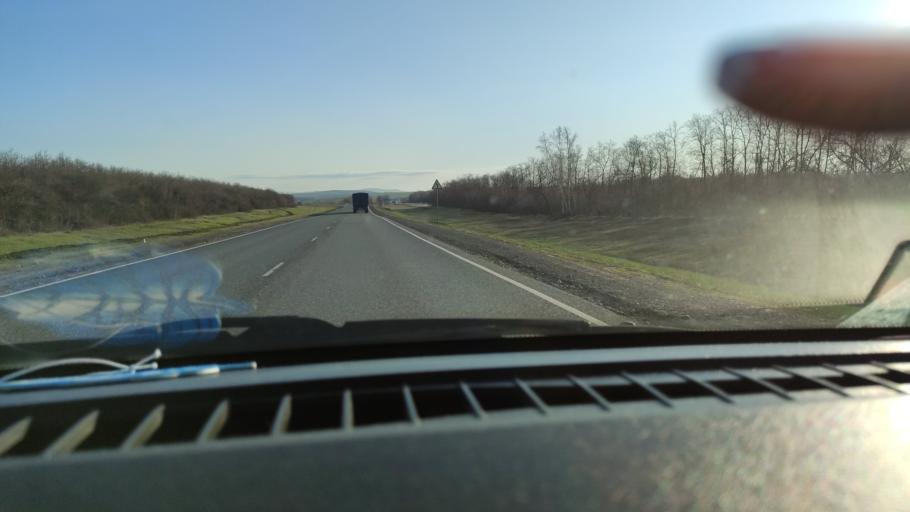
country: RU
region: Saratov
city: Balakovo
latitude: 52.1052
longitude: 47.7419
